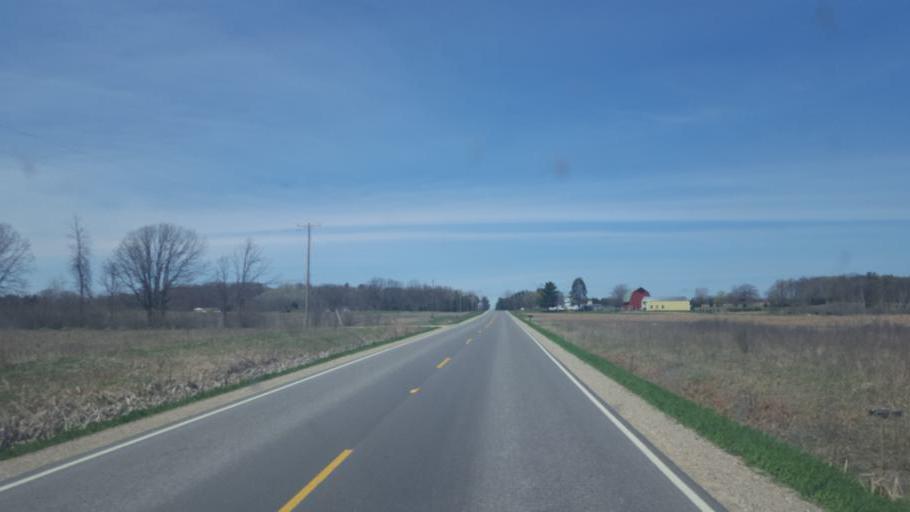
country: US
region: Michigan
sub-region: Gladwin County
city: Beaverton
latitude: 43.9116
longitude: -84.5852
